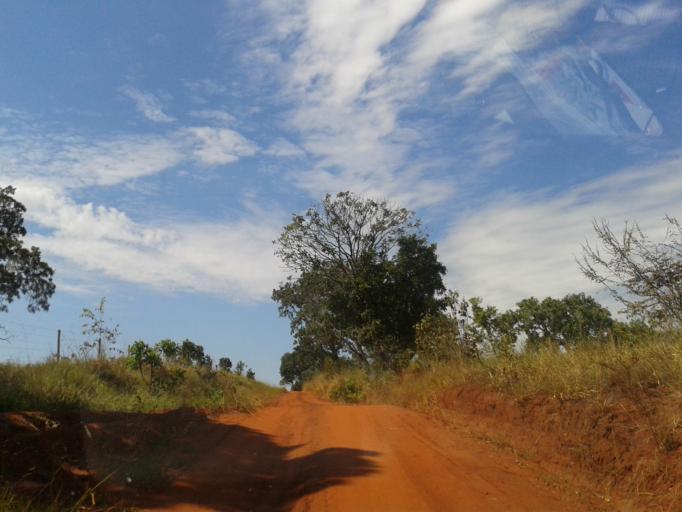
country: BR
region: Minas Gerais
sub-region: Campina Verde
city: Campina Verde
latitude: -19.4020
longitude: -49.7668
